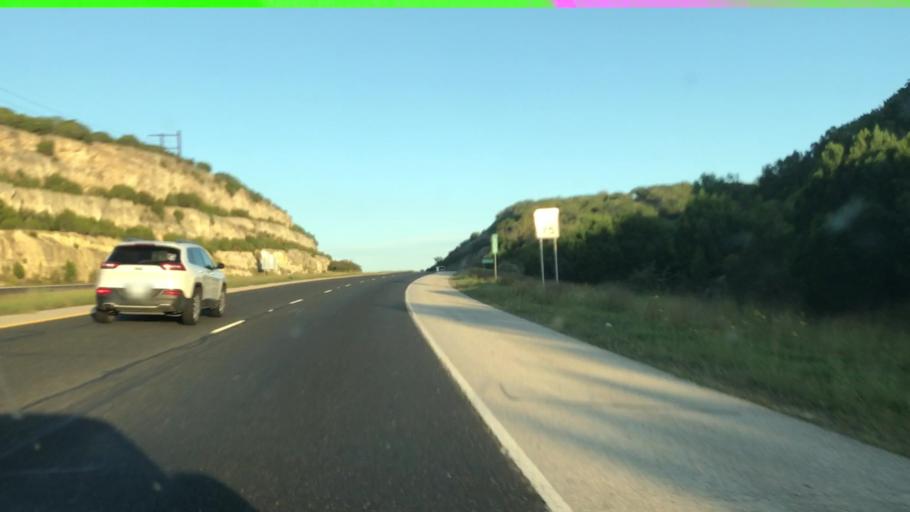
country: US
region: Texas
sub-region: Kerr County
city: Kerrville
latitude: 30.0702
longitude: -99.1013
